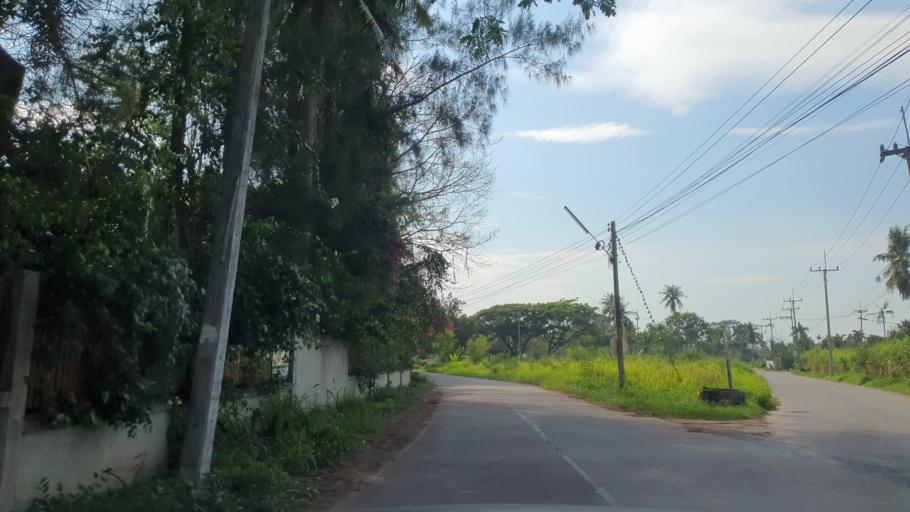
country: TH
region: Chon Buri
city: Sattahip
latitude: 12.7922
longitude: 100.9390
